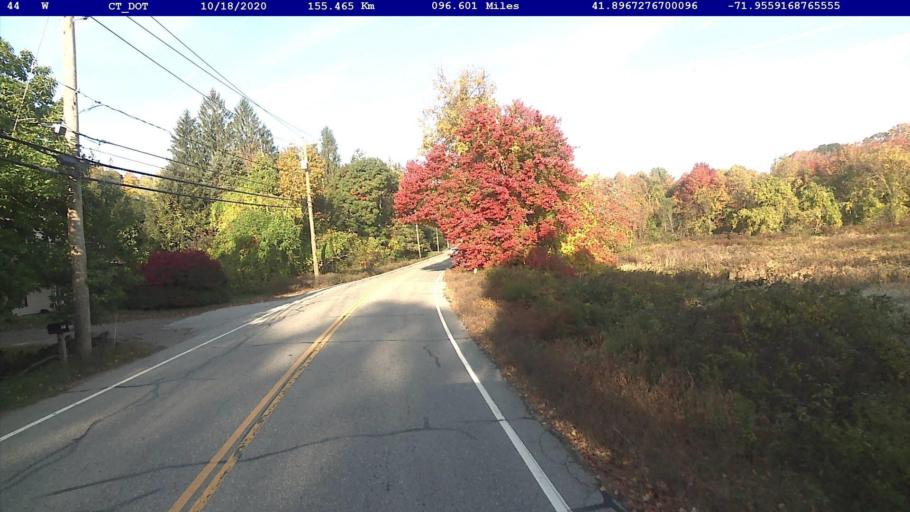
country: US
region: Connecticut
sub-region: Windham County
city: South Woodstock
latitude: 41.8968
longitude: -71.9559
